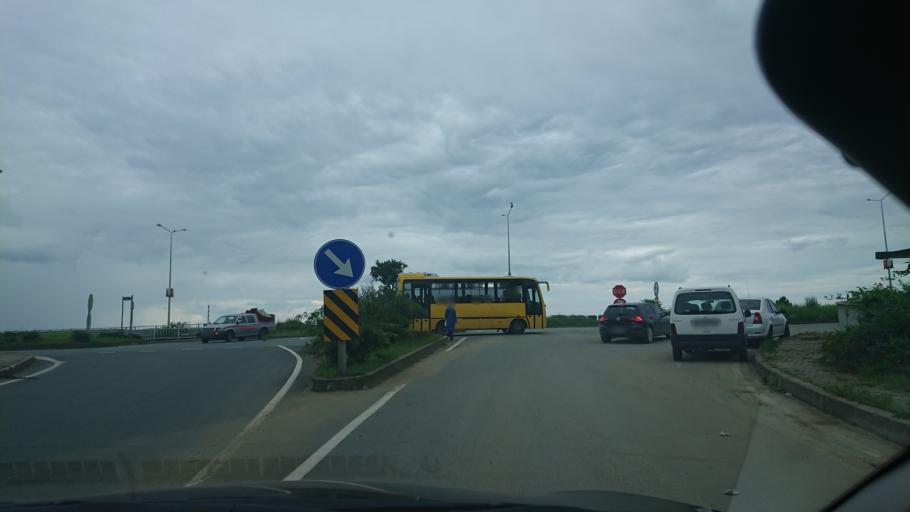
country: TR
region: Rize
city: Rize
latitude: 41.0346
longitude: 40.4799
